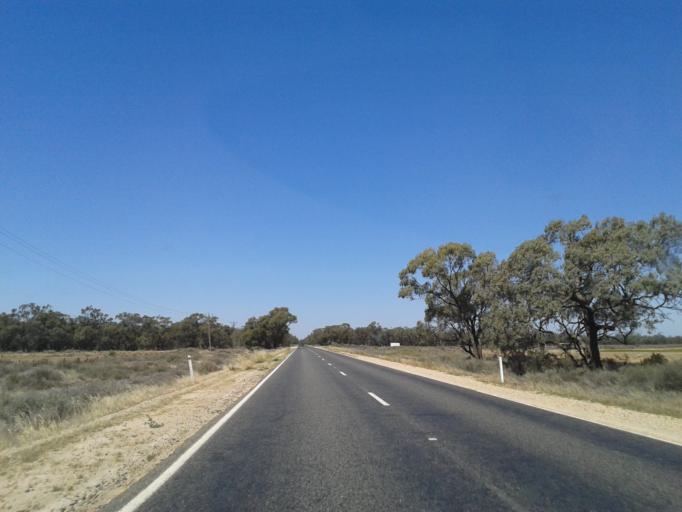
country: AU
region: Victoria
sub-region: Swan Hill
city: Swan Hill
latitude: -34.7132
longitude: 143.0985
